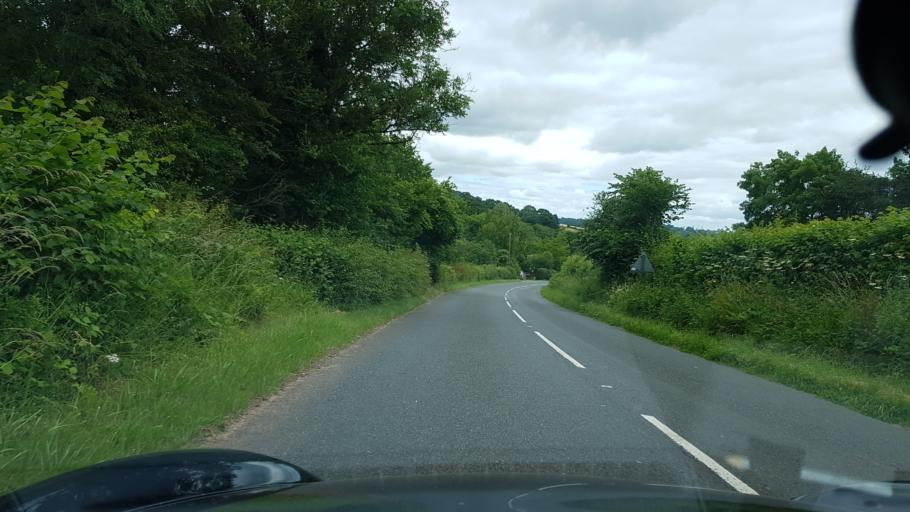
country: GB
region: Wales
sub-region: Monmouthshire
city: Grosmont
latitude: 51.8692
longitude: -2.8361
